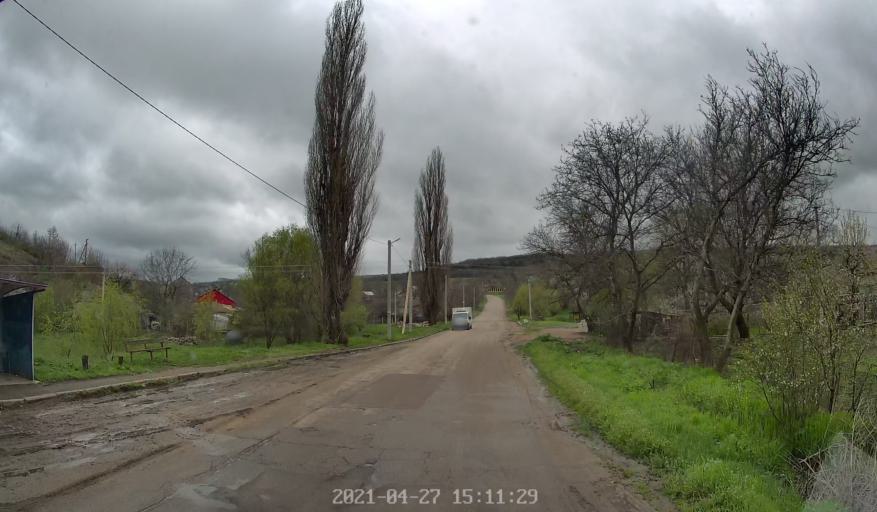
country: MD
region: Chisinau
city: Vadul lui Voda
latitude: 47.0314
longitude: 29.0270
